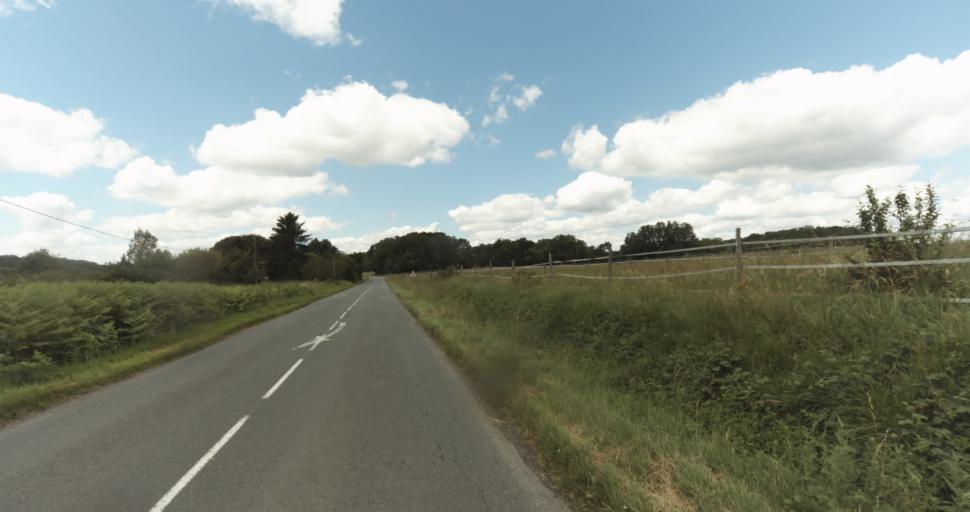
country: FR
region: Aquitaine
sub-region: Departement de la Dordogne
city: Beaumont-du-Perigord
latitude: 44.6914
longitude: 0.8772
